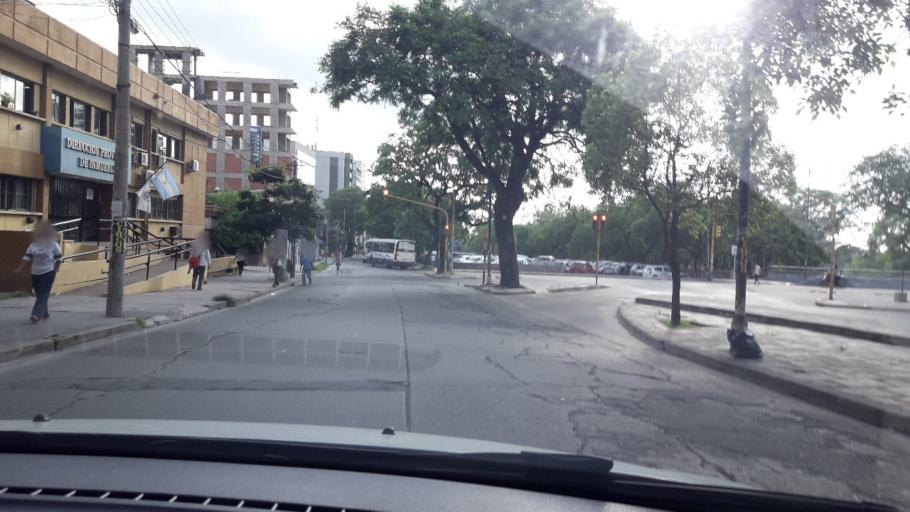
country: AR
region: Jujuy
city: San Salvador de Jujuy
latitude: -24.1888
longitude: -65.3018
